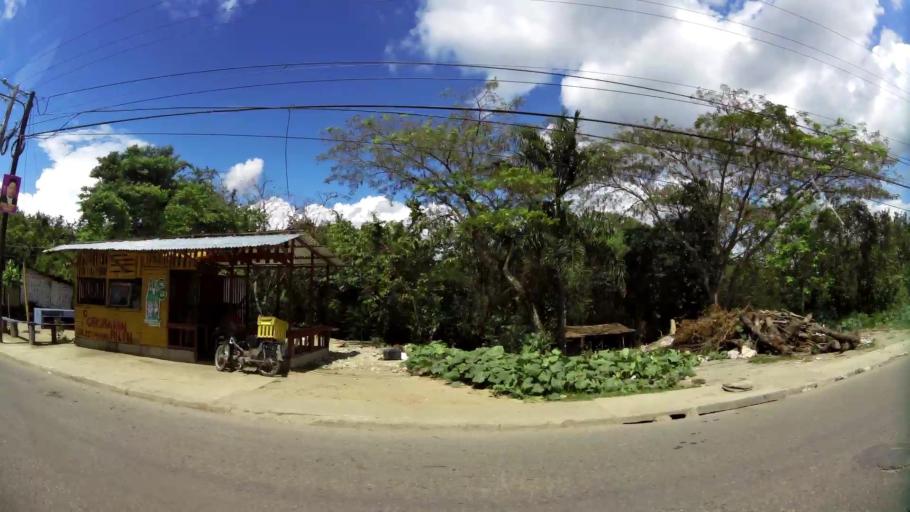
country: DO
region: Santiago
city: Santiago de los Caballeros
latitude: 19.4133
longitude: -70.6761
